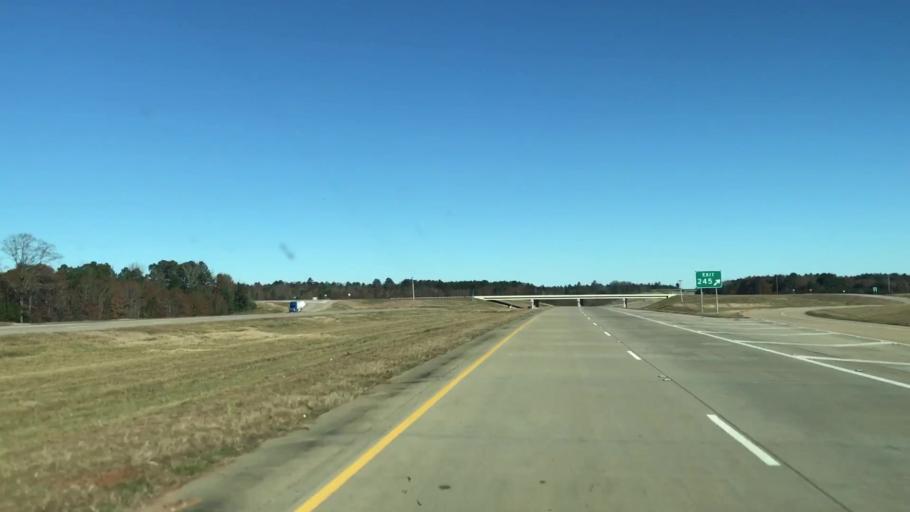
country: US
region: Louisiana
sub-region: Caddo Parish
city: Vivian
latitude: 32.9925
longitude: -93.9104
